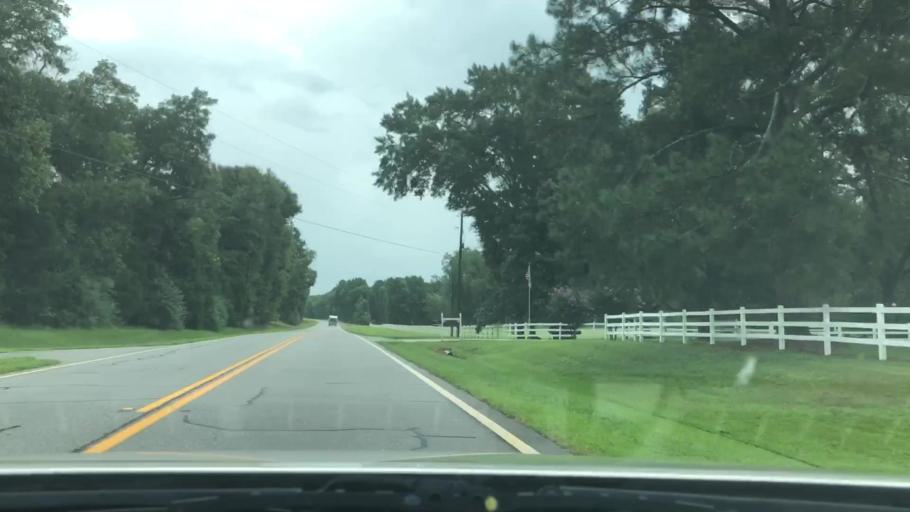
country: US
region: Georgia
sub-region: Pike County
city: Zebulon
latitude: 33.0873
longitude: -84.2714
